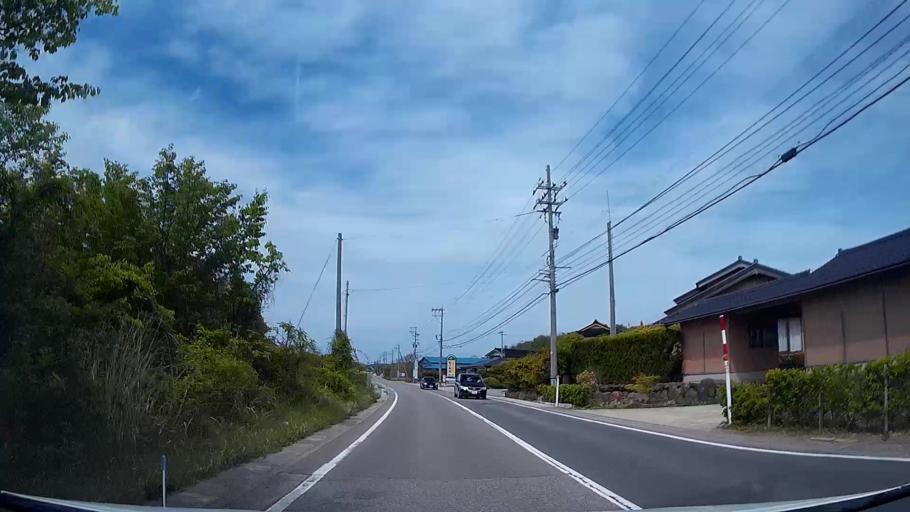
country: JP
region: Ishikawa
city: Hakui
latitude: 36.9733
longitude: 136.7748
